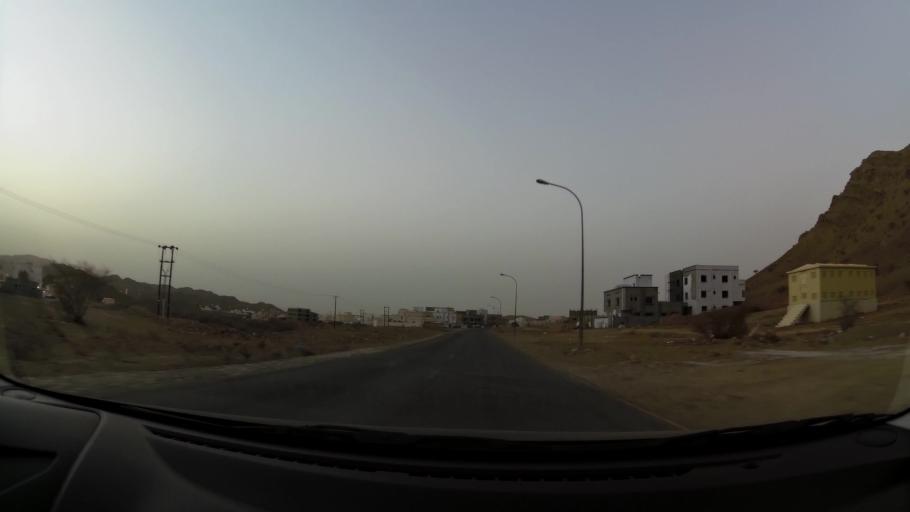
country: OM
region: Muhafazat Masqat
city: Bawshar
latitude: 23.5010
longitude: 58.3446
